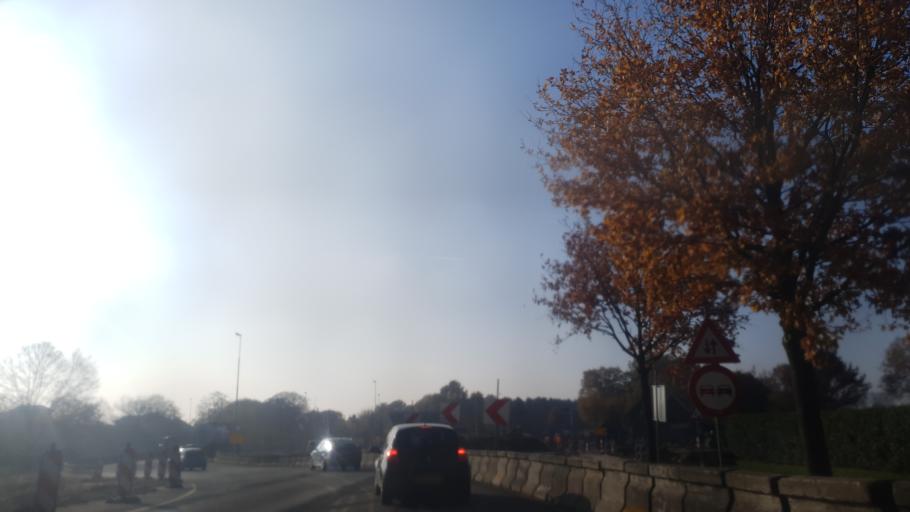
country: NL
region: North Brabant
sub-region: Gemeente Grave
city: Grave
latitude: 51.7497
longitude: 5.7304
